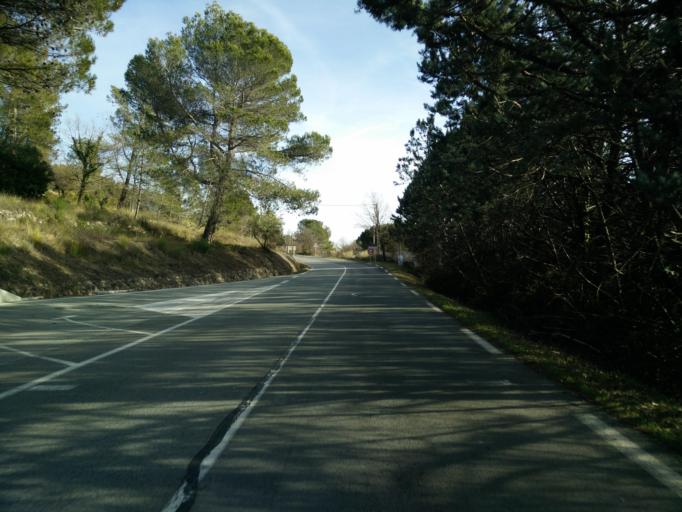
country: FR
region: Provence-Alpes-Cote d'Azur
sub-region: Departement du Var
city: Montauroux
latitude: 43.5975
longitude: 6.7905
